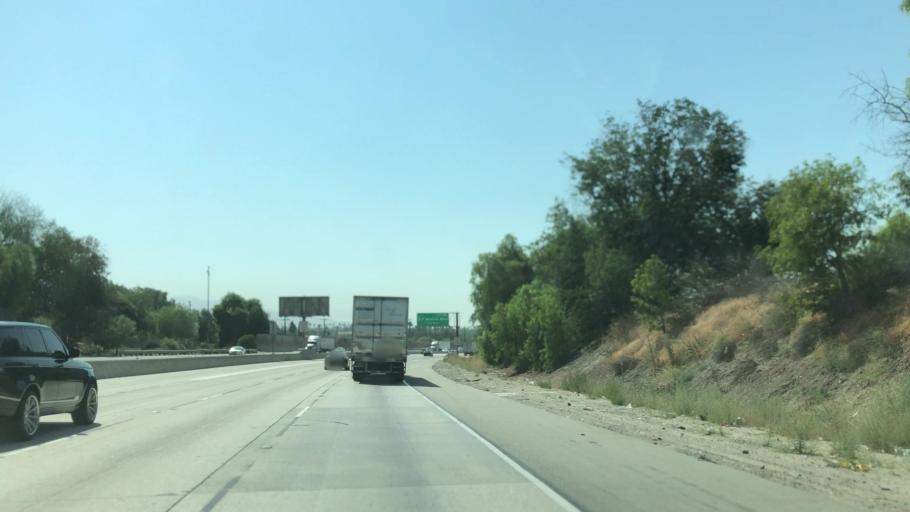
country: US
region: California
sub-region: Los Angeles County
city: San Fernando
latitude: 34.2855
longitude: -118.4606
